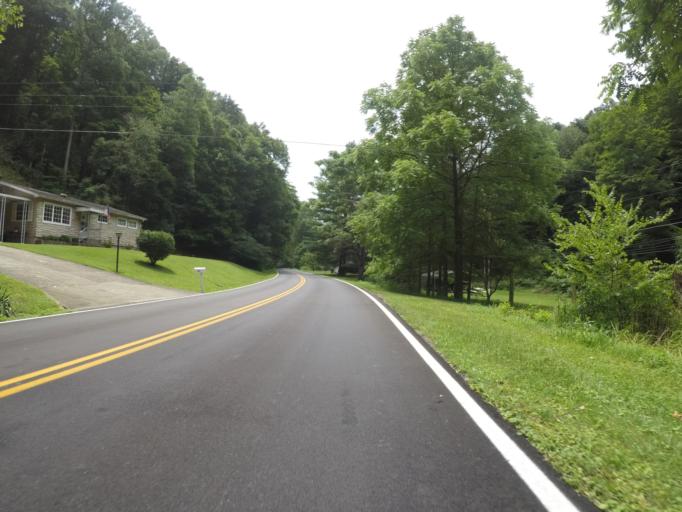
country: US
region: Kentucky
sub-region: Boyd County
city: Catlettsburg
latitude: 38.4256
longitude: -82.6275
